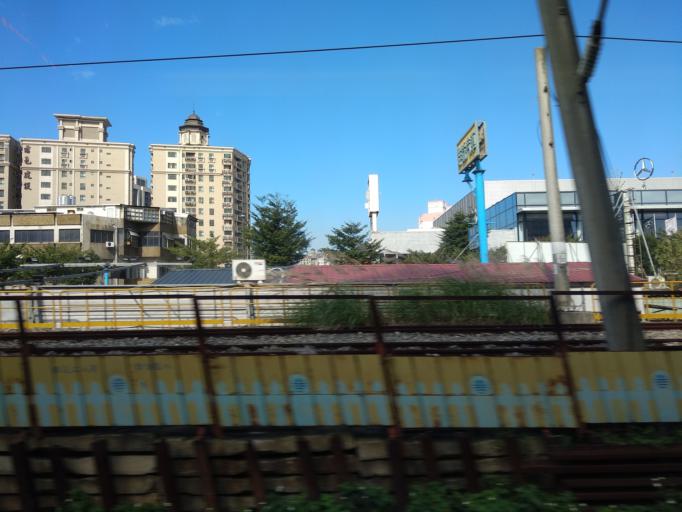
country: TW
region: Taiwan
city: Taoyuan City
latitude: 24.9789
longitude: 121.2729
